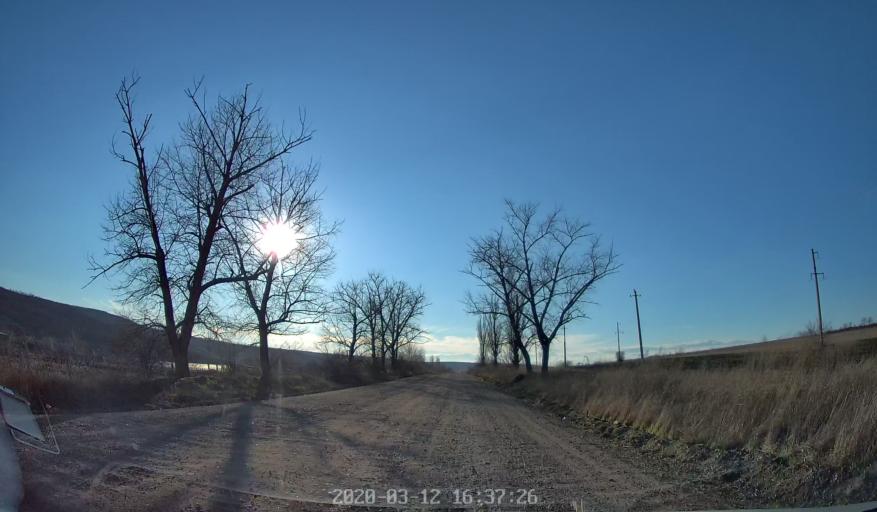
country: MD
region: Anenii Noi
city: Anenii Noi
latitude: 46.8154
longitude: 29.1882
